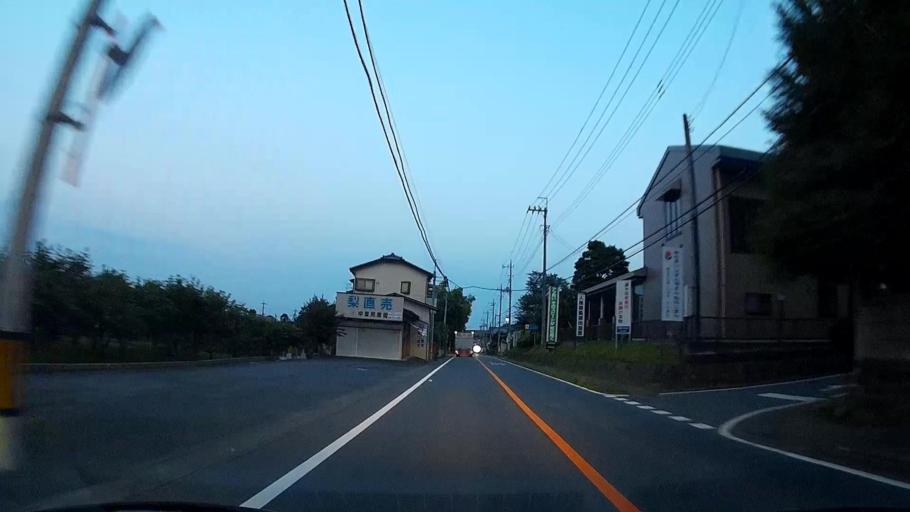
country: JP
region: Gunma
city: Annaka
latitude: 36.3730
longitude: 138.9001
